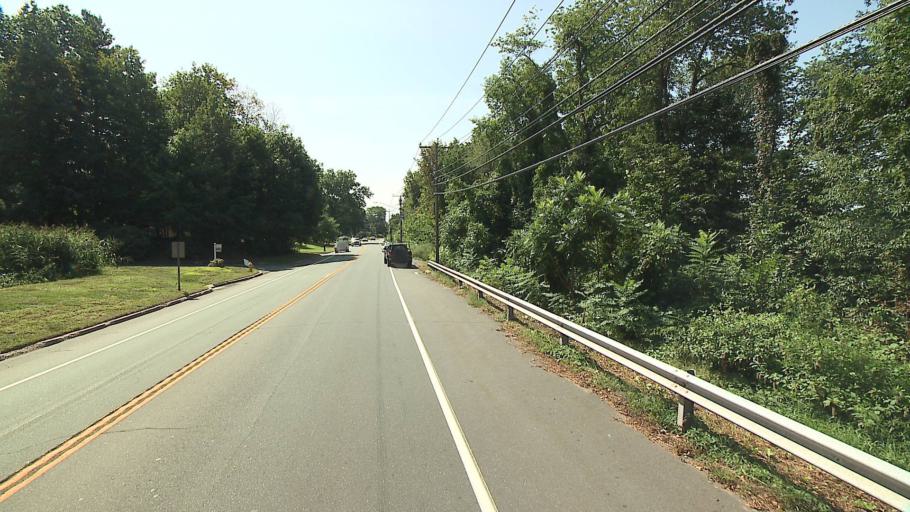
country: US
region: Connecticut
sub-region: Hartford County
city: Windsor Locks
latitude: 41.9254
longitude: -72.6063
